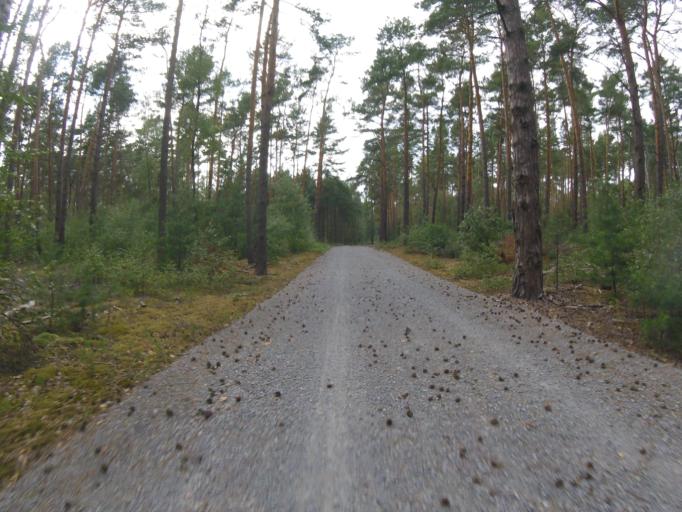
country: DE
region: Brandenburg
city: Halbe
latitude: 52.1514
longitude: 13.7489
